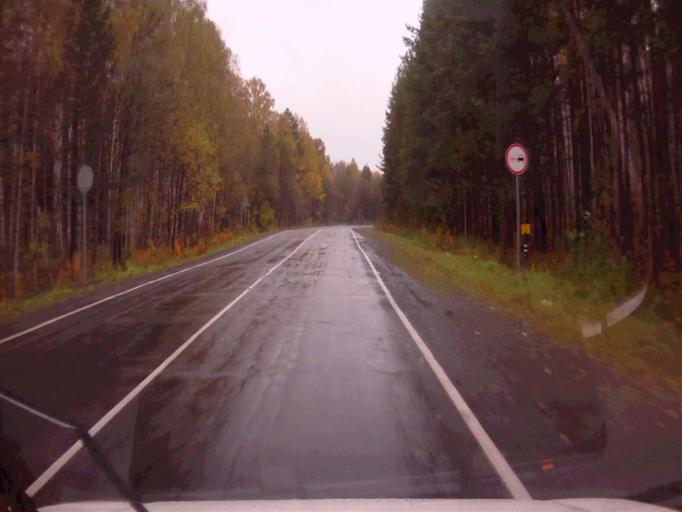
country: RU
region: Chelyabinsk
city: Verkhniy Ufaley
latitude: 55.9521
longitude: 60.3969
